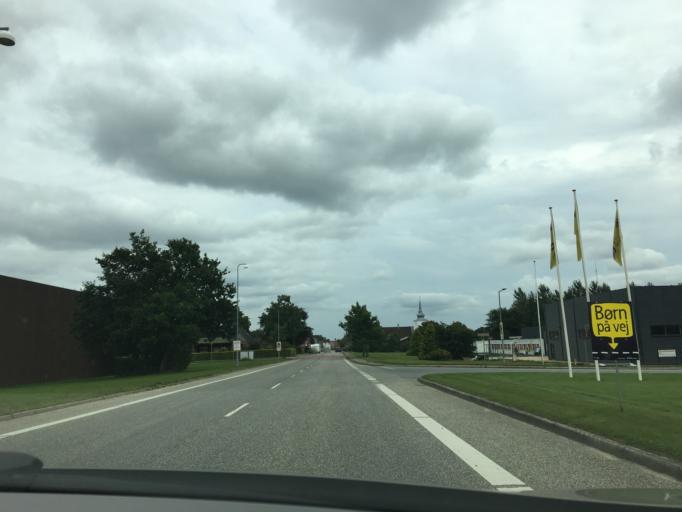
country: DK
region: South Denmark
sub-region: Vejle Kommune
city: Jelling
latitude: 55.7024
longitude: 9.3746
